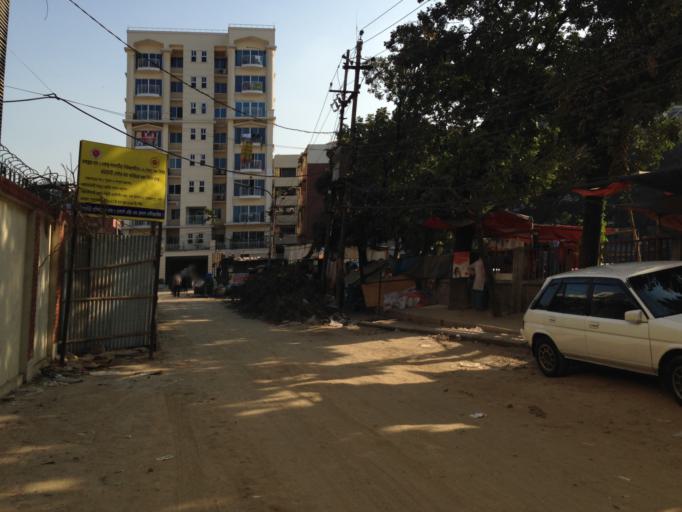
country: BD
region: Dhaka
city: Azimpur
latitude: 23.7587
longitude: 90.3729
